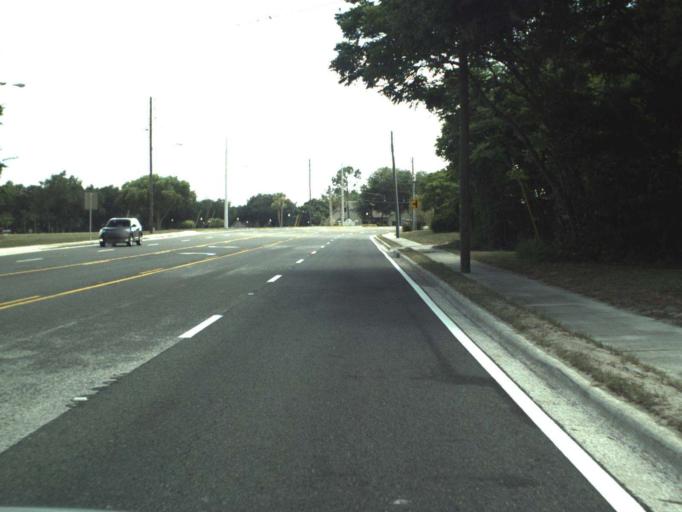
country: US
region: Florida
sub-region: Lake County
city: Leesburg
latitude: 28.8080
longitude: -81.8593
